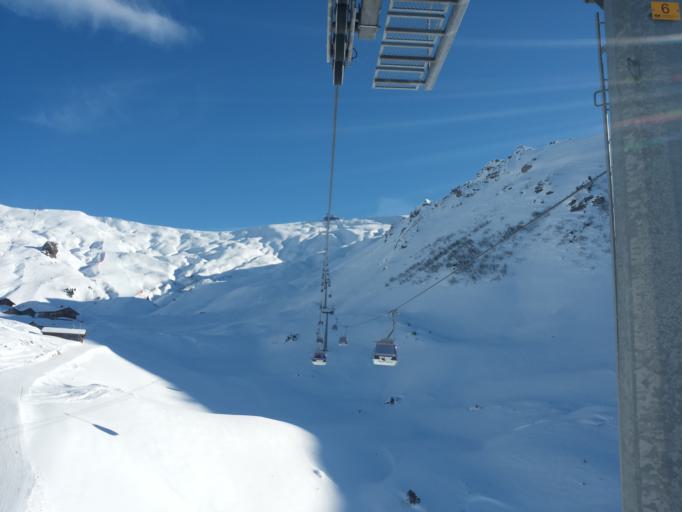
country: CH
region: Bern
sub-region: Interlaken-Oberhasli District
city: Meiringen
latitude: 46.7466
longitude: 8.2421
